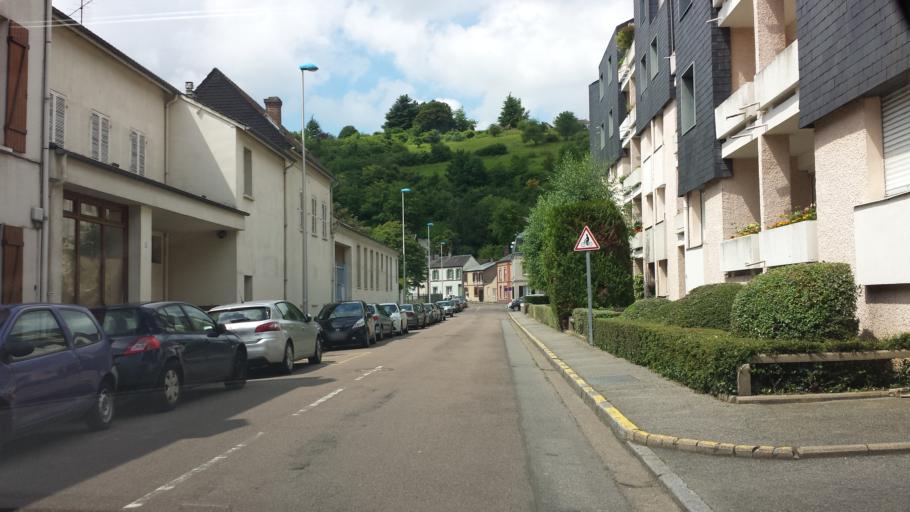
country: FR
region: Haute-Normandie
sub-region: Departement de l'Eure
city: Evreux
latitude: 49.0293
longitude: 1.1484
